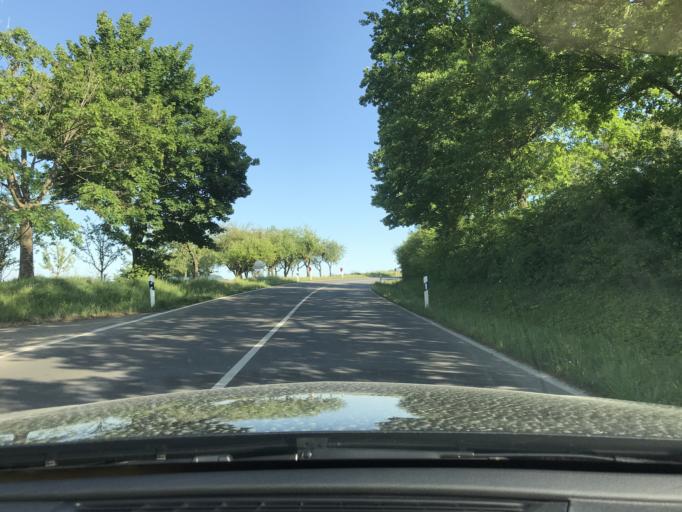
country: DE
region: Baden-Wuerttemberg
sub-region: Regierungsbezirk Stuttgart
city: Schwaikheim
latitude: 48.8773
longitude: 9.3191
